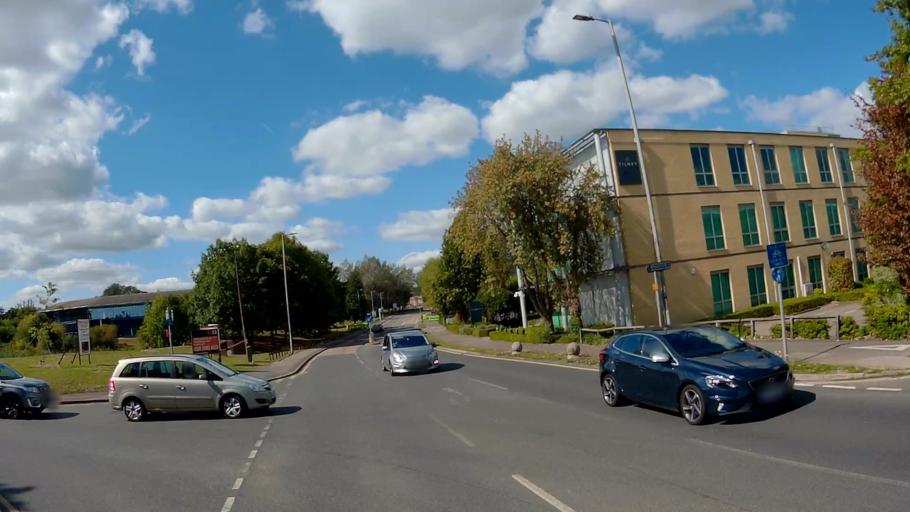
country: GB
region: England
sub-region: Bracknell Forest
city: Bracknell
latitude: 51.4172
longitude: -0.7707
